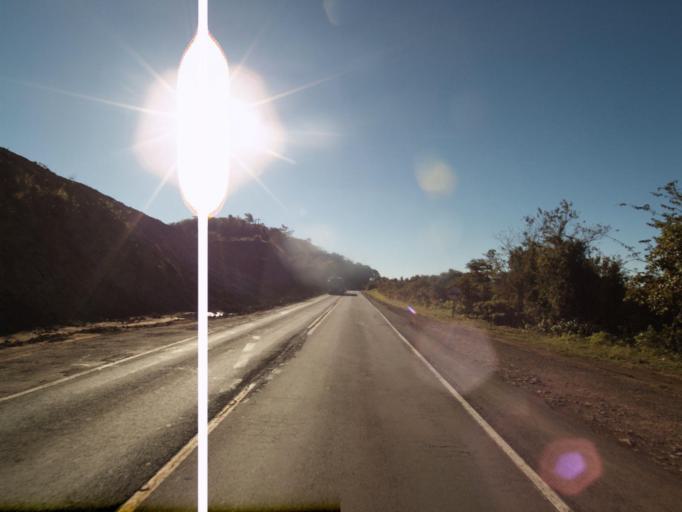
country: AR
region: Misiones
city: Bernardo de Irigoyen
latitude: -26.4908
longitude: -53.5031
